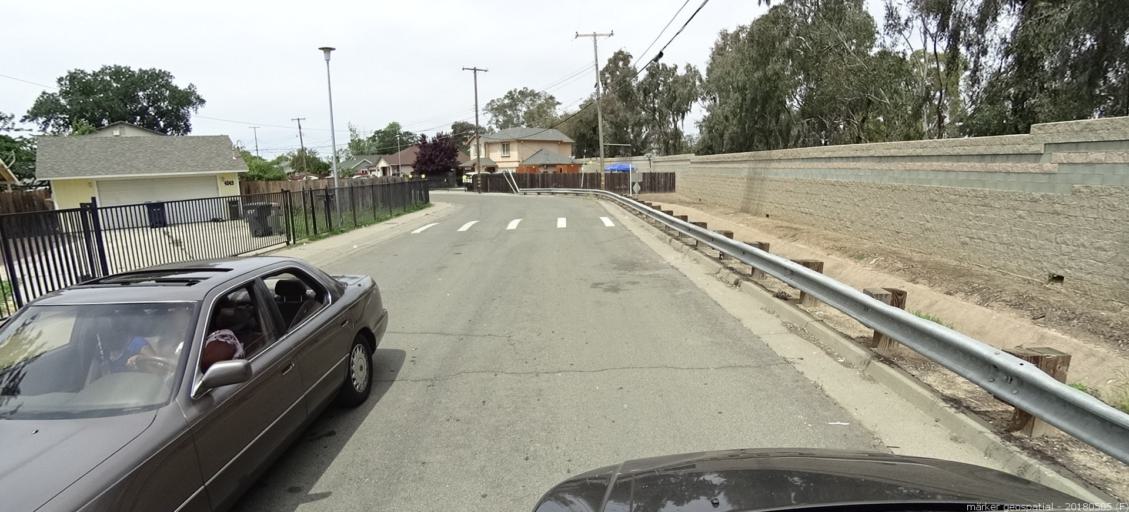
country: US
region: California
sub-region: Sacramento County
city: Rio Linda
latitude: 38.6419
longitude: -121.4308
